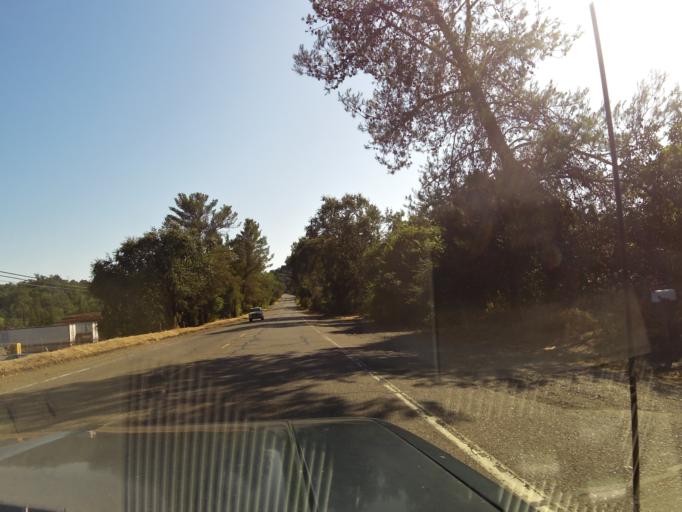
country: US
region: California
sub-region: Sonoma County
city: Cloverdale
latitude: 38.8232
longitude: -123.0187
